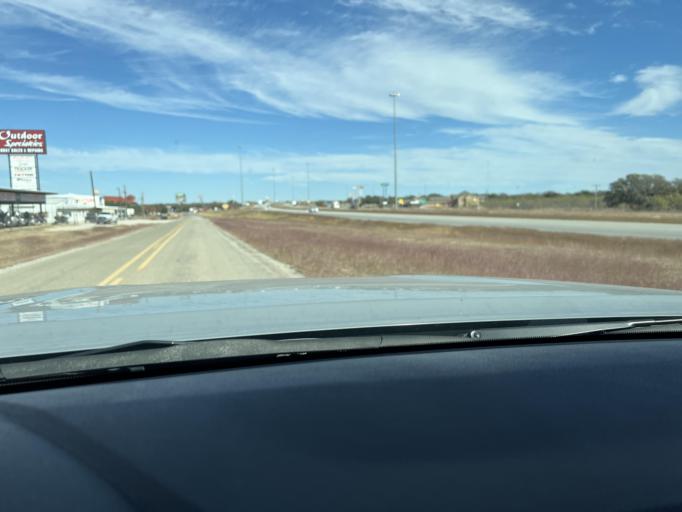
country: US
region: Texas
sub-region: Eastland County
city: Eastland
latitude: 32.3963
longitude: -98.7942
